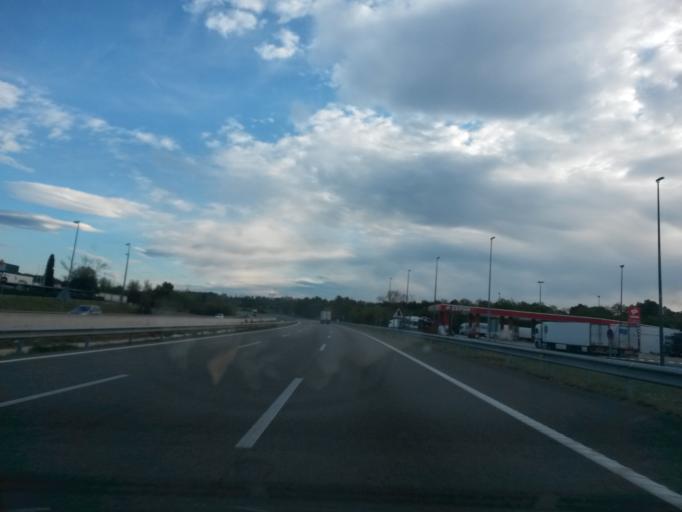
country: ES
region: Catalonia
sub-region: Provincia de Girona
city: Pontos
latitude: 42.1730
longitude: 2.9307
